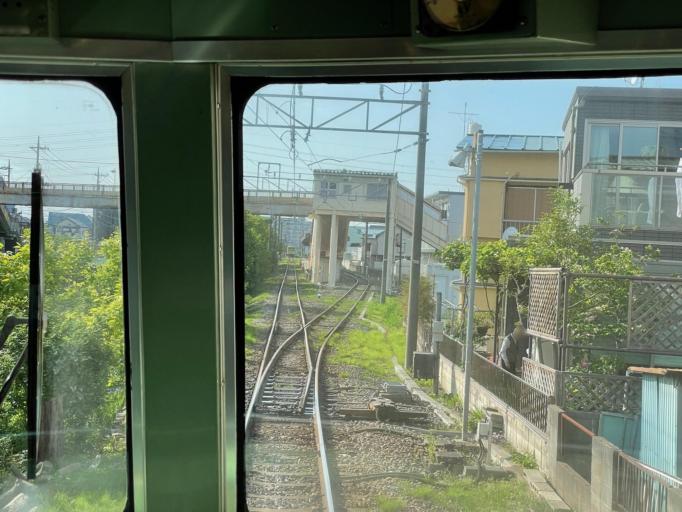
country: JP
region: Chiba
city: Nagareyama
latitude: 35.8352
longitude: 139.9180
